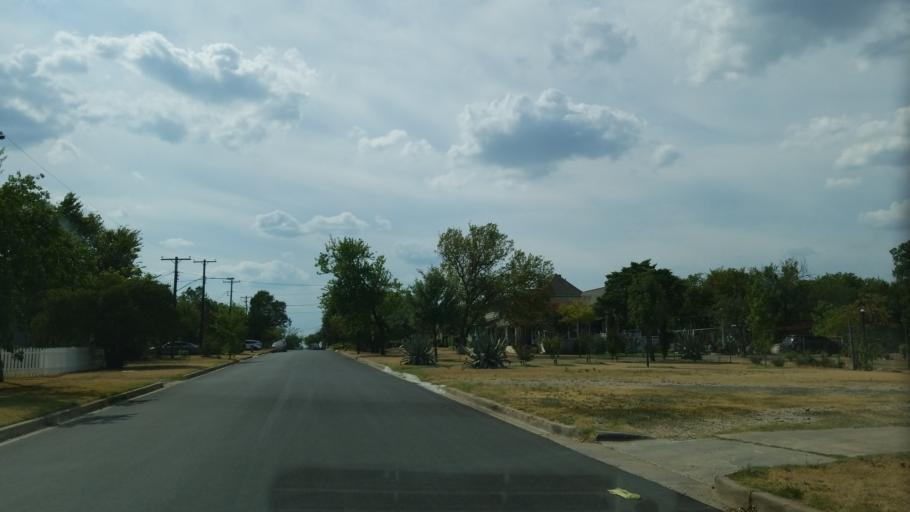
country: US
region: Texas
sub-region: Dallas County
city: Dallas
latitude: 32.7704
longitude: -96.8421
